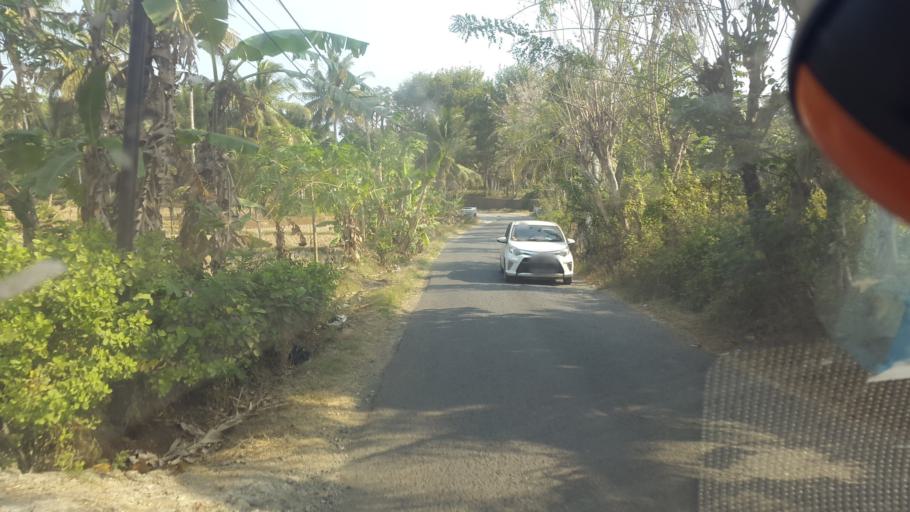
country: ID
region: West Java
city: Babakan Baru
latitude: -7.3117
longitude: 106.6208
